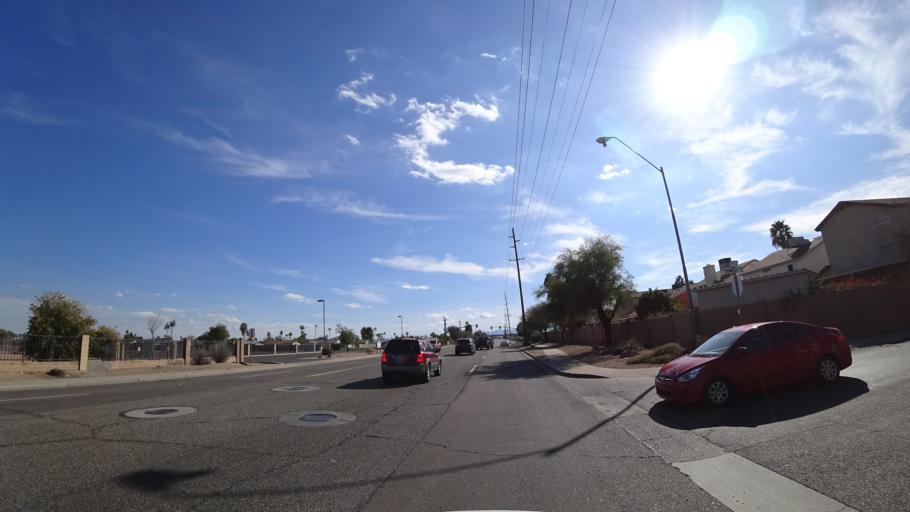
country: US
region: Arizona
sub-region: Maricopa County
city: Peoria
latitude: 33.5755
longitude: -112.2204
